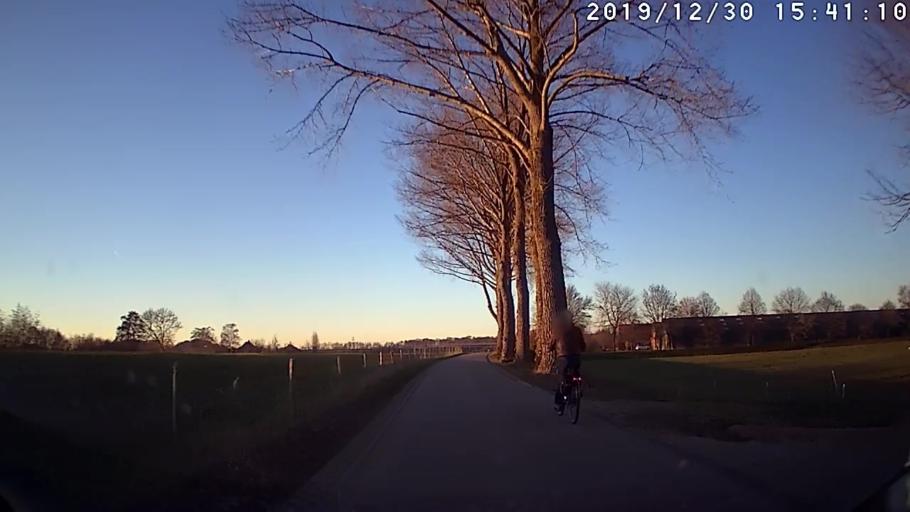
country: NL
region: Overijssel
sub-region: Gemeente Zwolle
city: Zwolle
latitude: 52.4675
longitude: 6.1445
